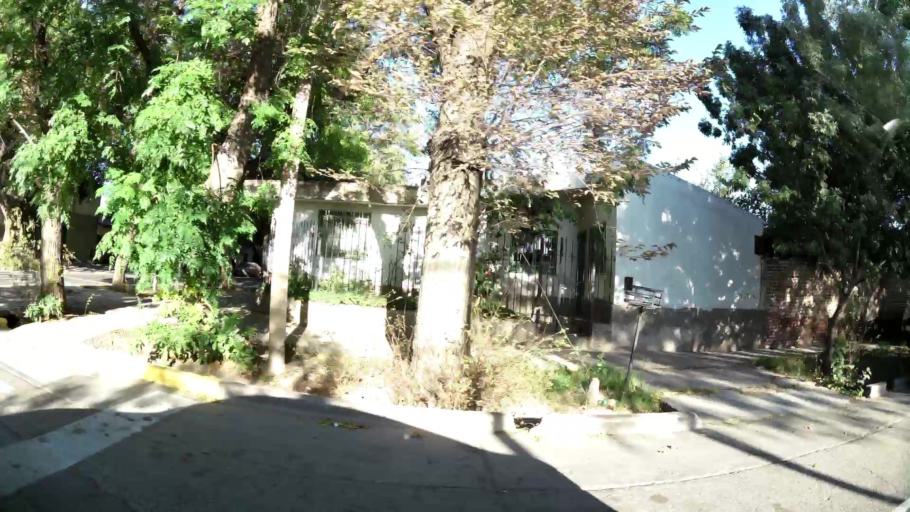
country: AR
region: Mendoza
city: Mendoza
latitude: -32.8733
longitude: -68.8235
